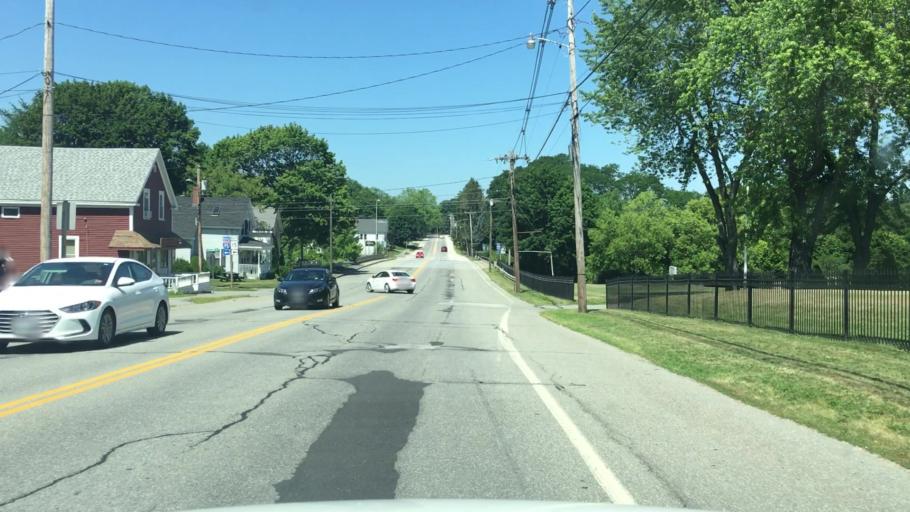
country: US
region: Maine
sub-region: Penobscot County
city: Bangor
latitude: 44.8109
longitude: -68.7893
